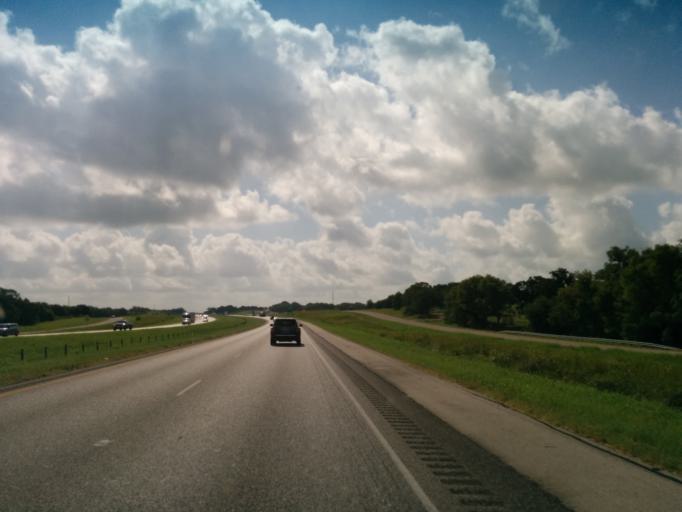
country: US
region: Texas
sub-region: Fayette County
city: Flatonia
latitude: 29.6920
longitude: -97.0109
